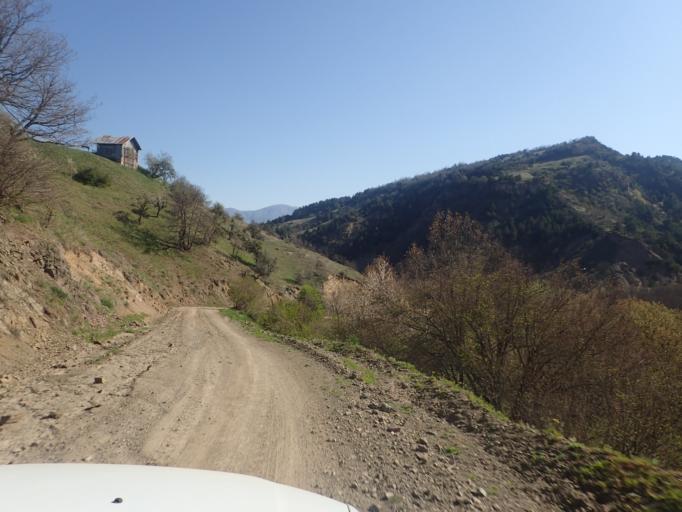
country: TR
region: Ordu
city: Mesudiye
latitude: 40.4185
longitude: 37.8232
